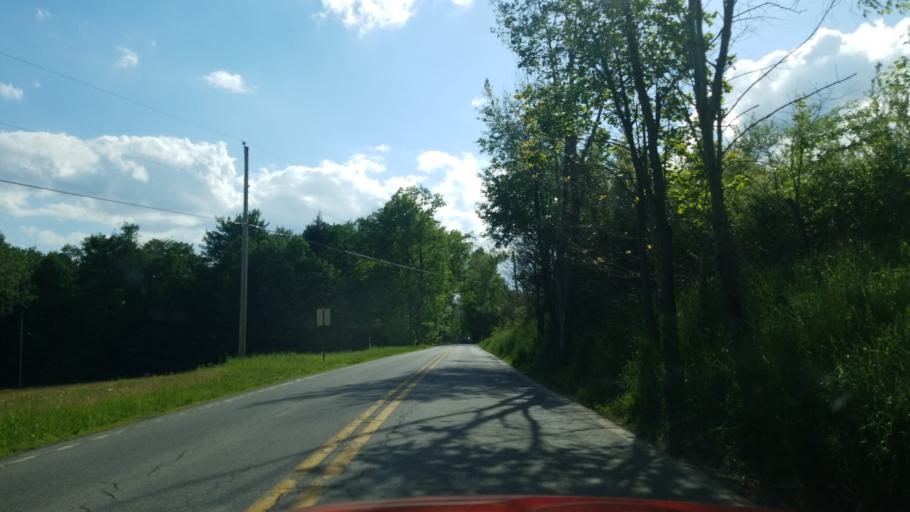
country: US
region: Pennsylvania
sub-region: Clearfield County
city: Hyde
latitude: 40.9780
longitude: -78.4723
